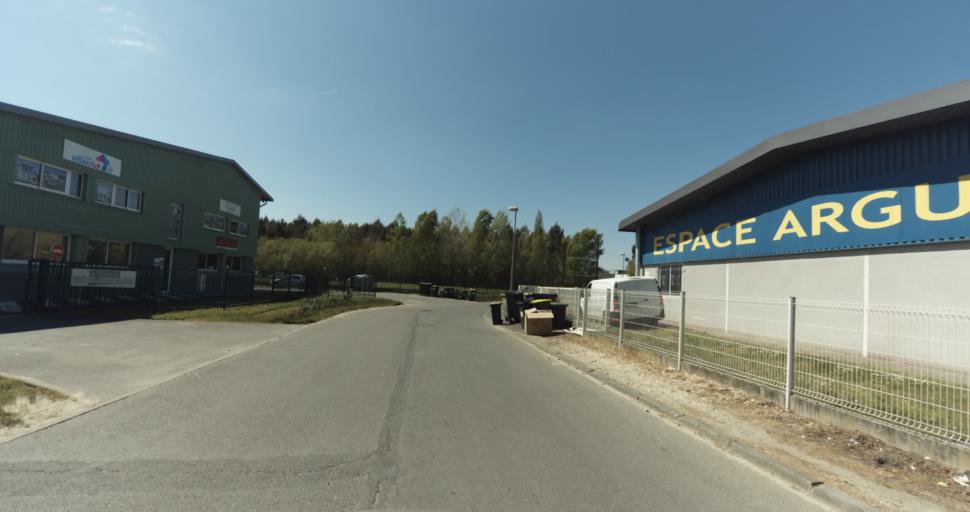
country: FR
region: Aquitaine
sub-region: Departement de la Gironde
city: Martignas-sur-Jalle
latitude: 44.8093
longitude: -0.7504
